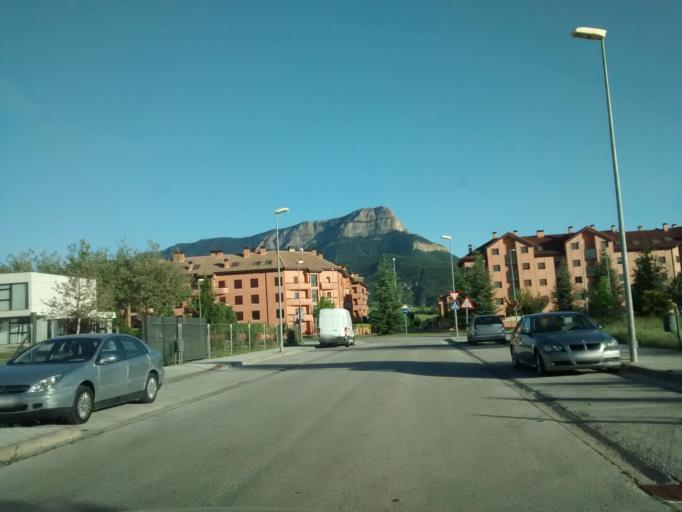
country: ES
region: Aragon
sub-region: Provincia de Huesca
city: Jaca
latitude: 42.5661
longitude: -0.5616
